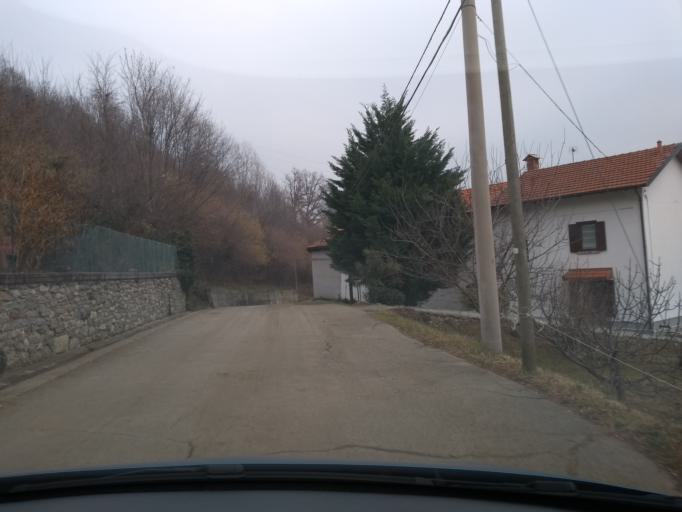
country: IT
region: Piedmont
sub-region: Provincia di Torino
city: Grosso
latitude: 45.2664
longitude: 7.5504
